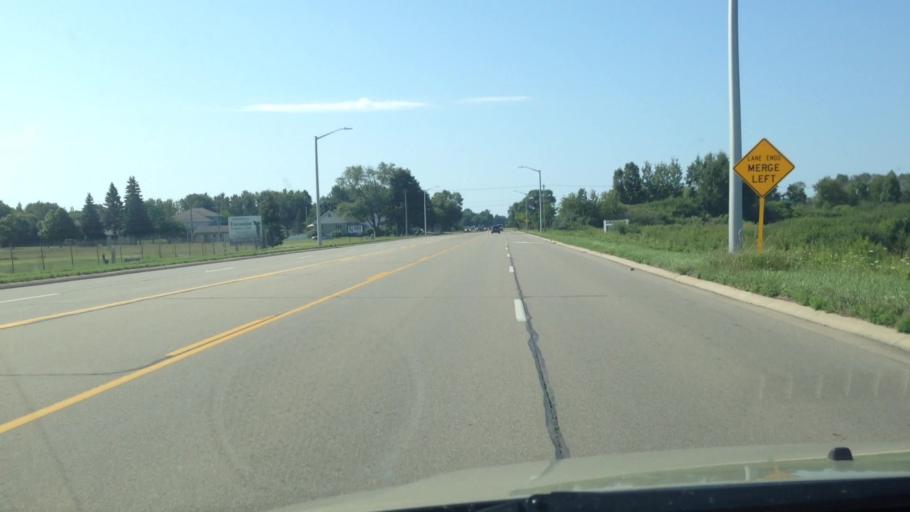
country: US
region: Michigan
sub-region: Delta County
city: Escanaba
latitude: 45.7266
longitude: -87.0801
